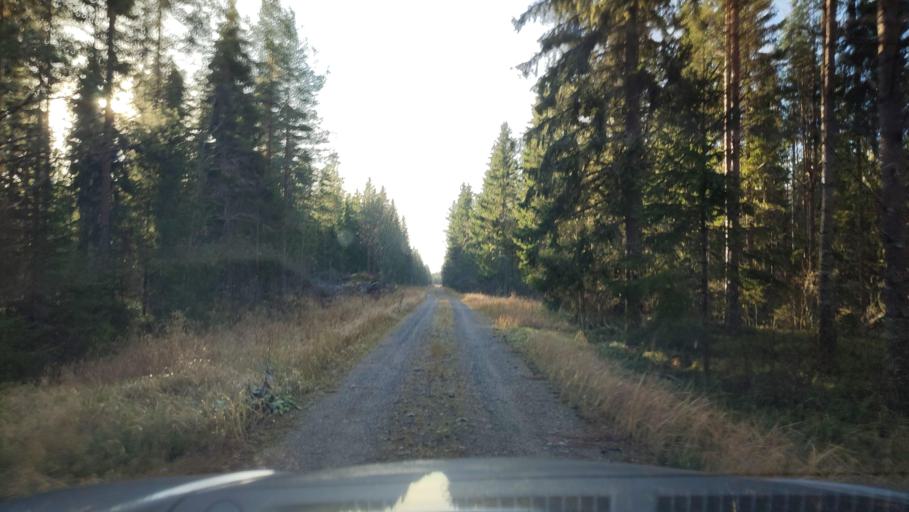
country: FI
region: Southern Ostrobothnia
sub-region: Suupohja
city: Karijoki
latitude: 62.1878
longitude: 21.6075
